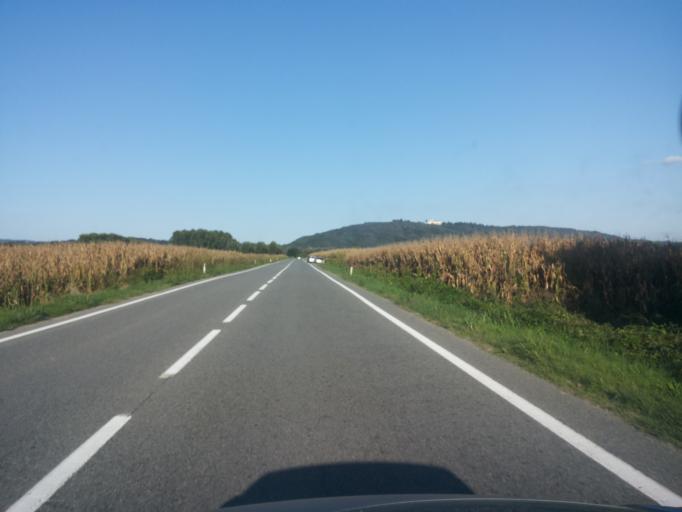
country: IT
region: Piedmont
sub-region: Provincia di Torino
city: Strambino
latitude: 45.3916
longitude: 7.9104
